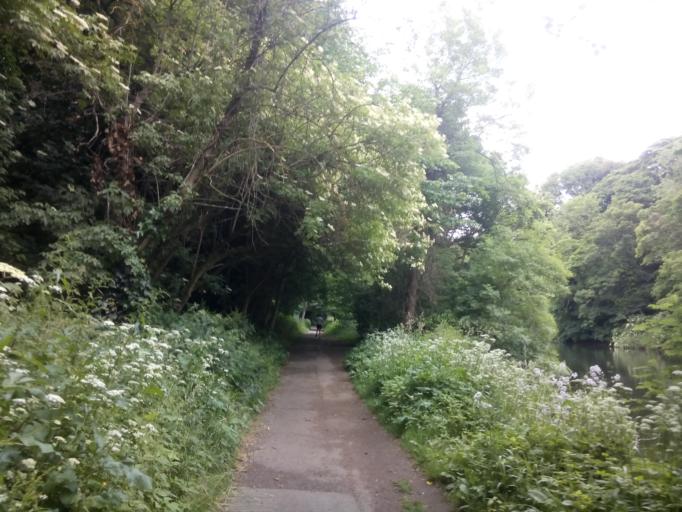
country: GB
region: England
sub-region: County Durham
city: Durham
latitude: 54.7708
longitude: -1.5752
